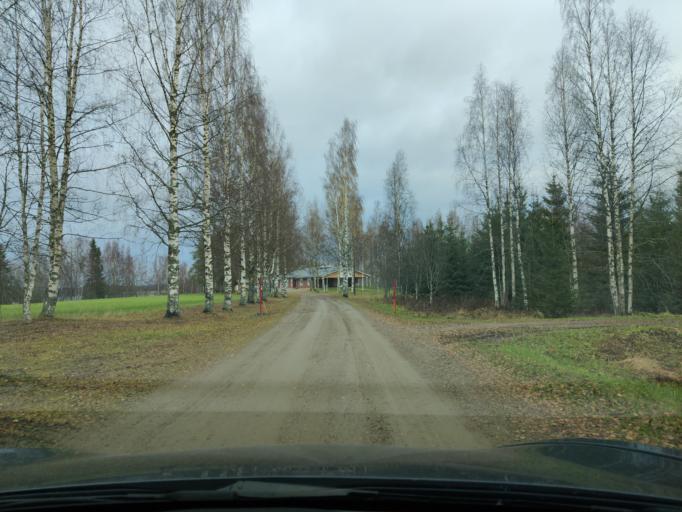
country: FI
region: Northern Savo
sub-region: Ylae-Savo
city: Kiuruvesi
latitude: 63.6405
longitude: 26.6548
